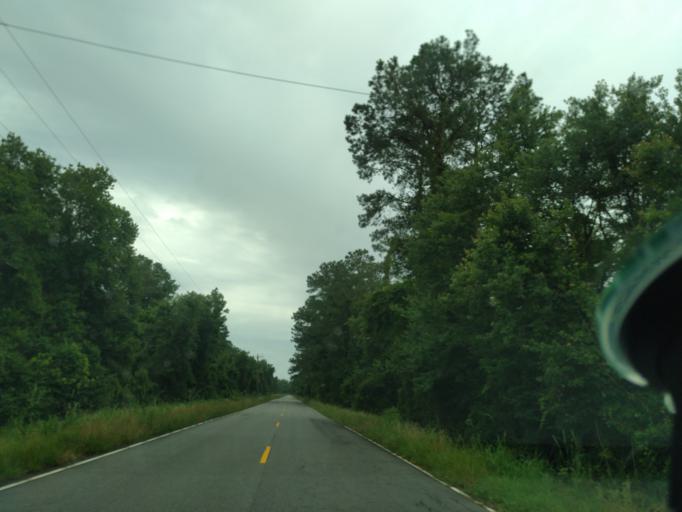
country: US
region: North Carolina
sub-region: Washington County
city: Plymouth
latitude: 35.7957
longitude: -76.5178
